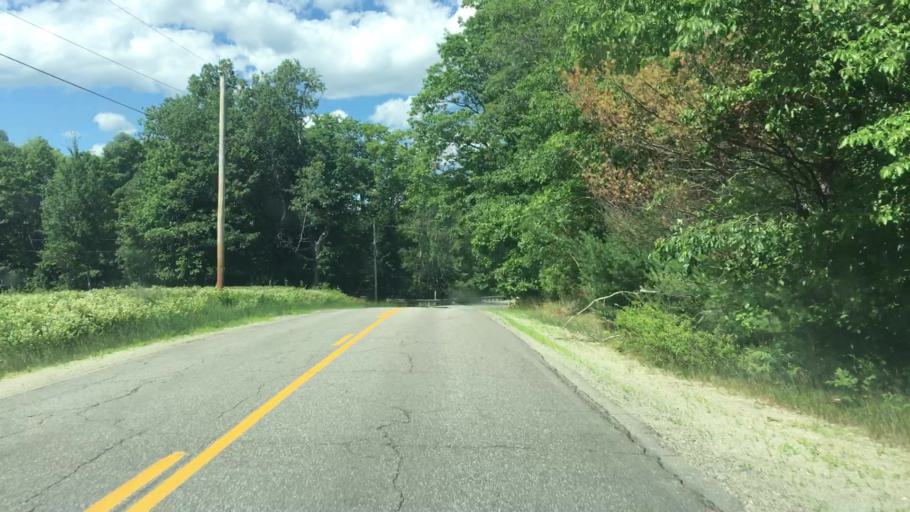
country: US
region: Maine
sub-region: Franklin County
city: Chesterville
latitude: 44.5856
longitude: -70.0887
